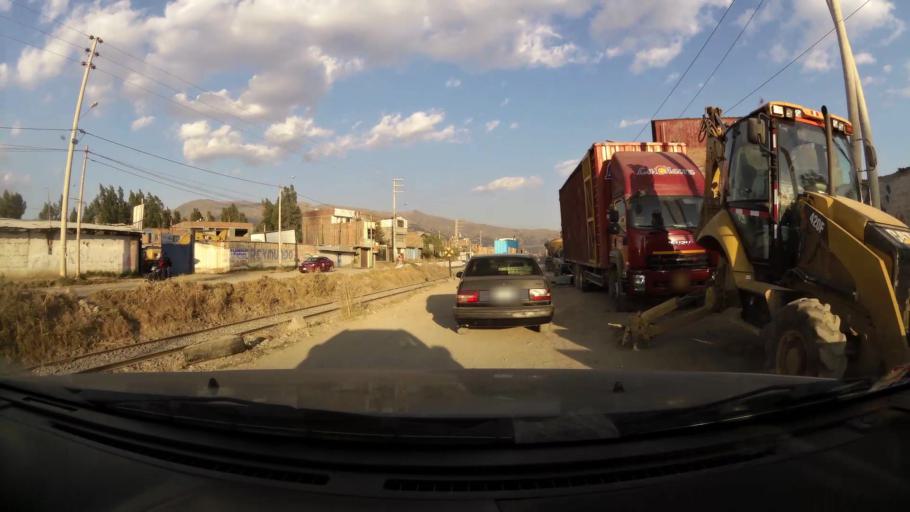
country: PE
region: Junin
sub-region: Provincia de Huancayo
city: El Tambo
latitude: -12.0409
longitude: -75.2231
